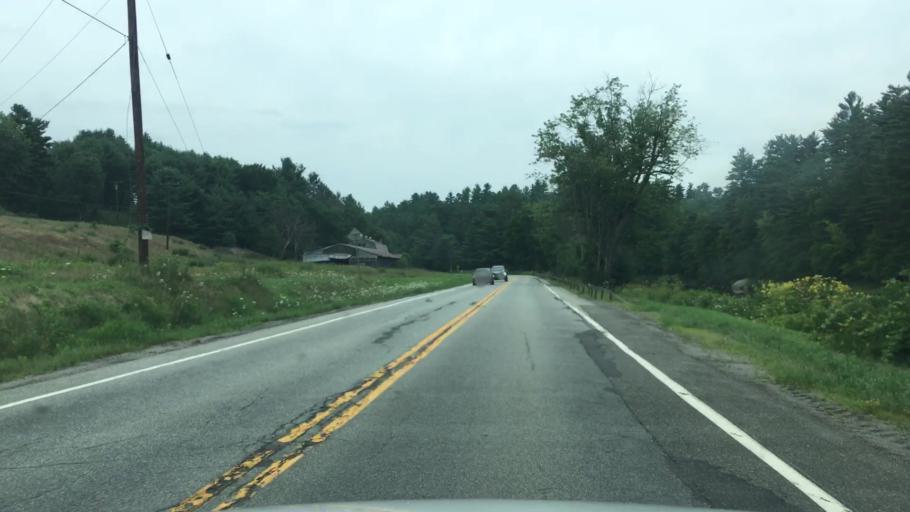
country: US
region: New York
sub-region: Essex County
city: Elizabethtown
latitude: 44.4151
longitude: -73.6804
